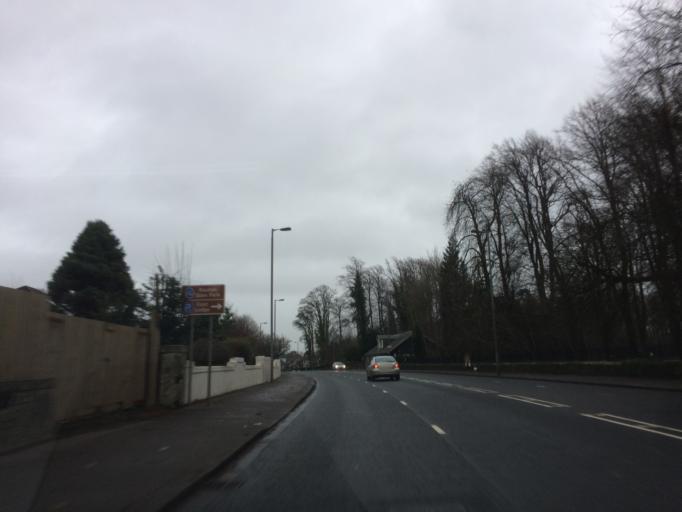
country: GB
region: Scotland
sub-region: East Renfrewshire
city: Giffnock
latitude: 55.7984
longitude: -4.3134
